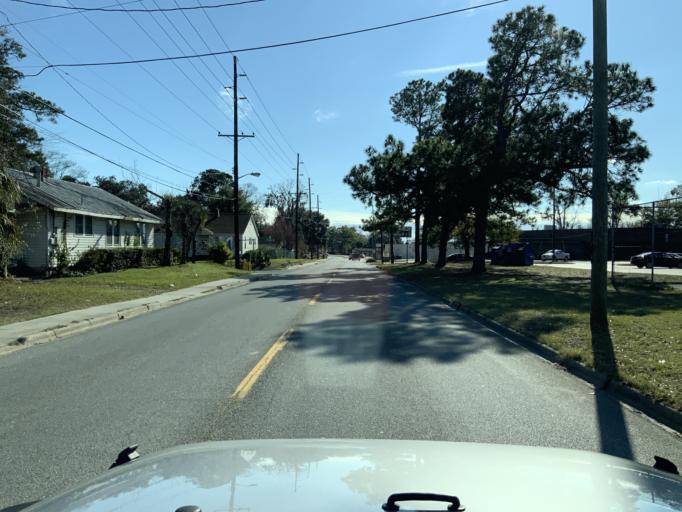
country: US
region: Georgia
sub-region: Chatham County
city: Thunderbolt
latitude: 32.0509
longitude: -81.0641
